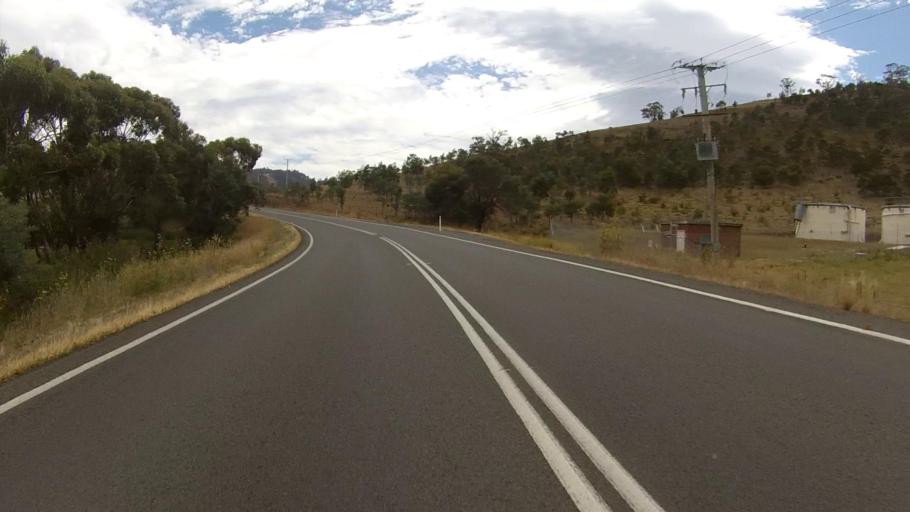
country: AU
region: Tasmania
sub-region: Brighton
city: Old Beach
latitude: -42.6834
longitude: 147.3538
